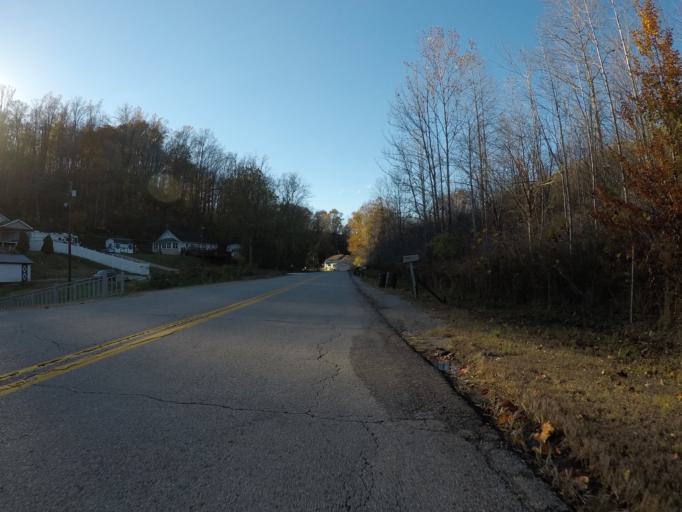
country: US
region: West Virginia
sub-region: Wayne County
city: Ceredo
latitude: 38.3903
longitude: -82.5677
